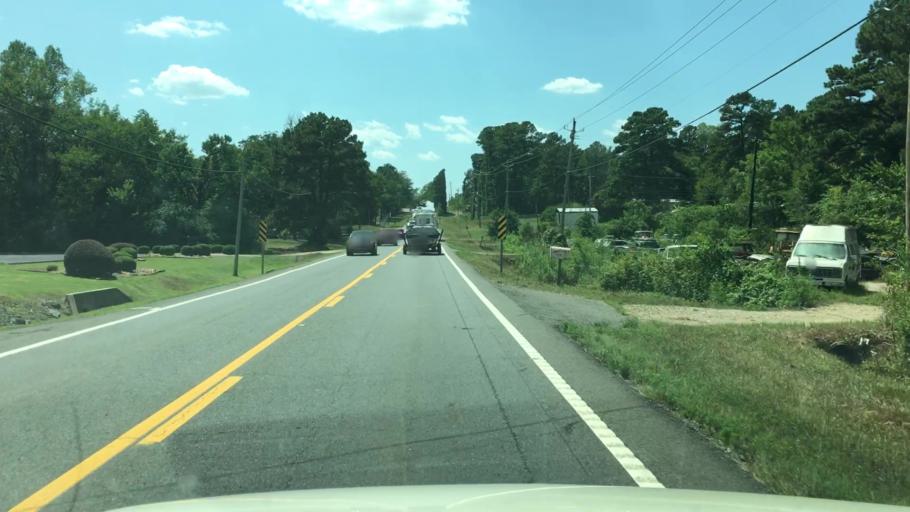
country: US
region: Arkansas
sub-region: Garland County
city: Piney
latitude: 34.5095
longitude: -93.1530
